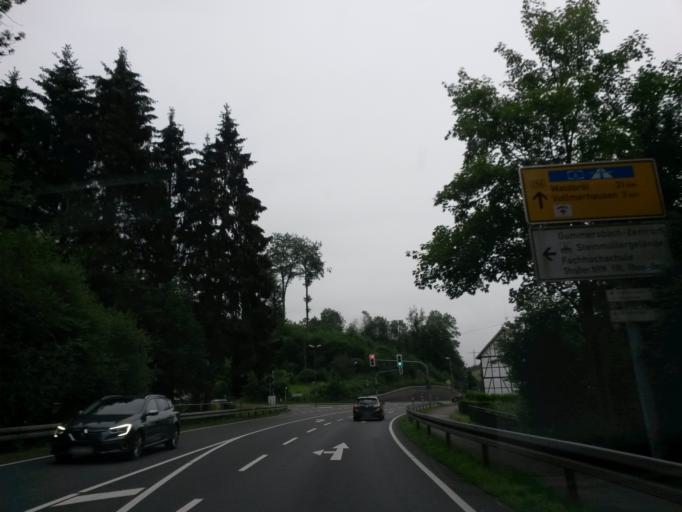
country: DE
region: North Rhine-Westphalia
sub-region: Regierungsbezirk Koln
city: Gummersbach
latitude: 51.0146
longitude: 7.5582
